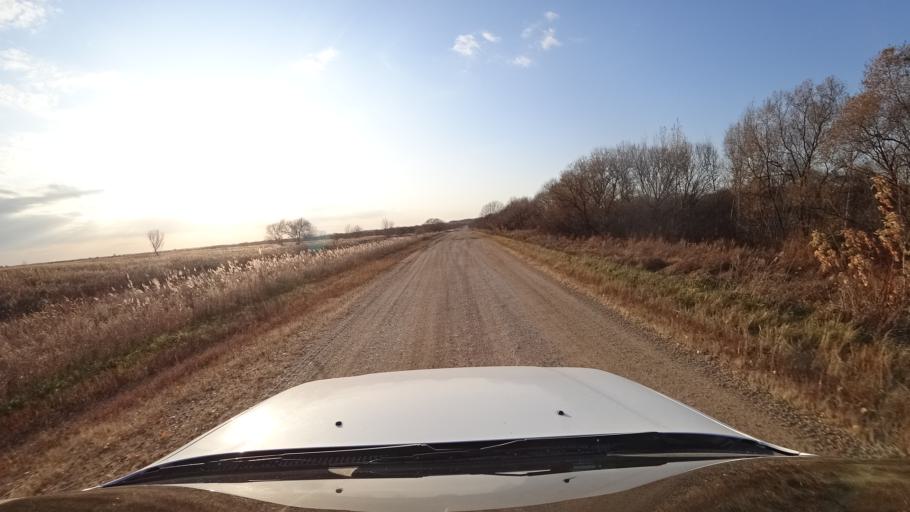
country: RU
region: Primorskiy
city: Lazo
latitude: 45.8253
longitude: 133.6077
